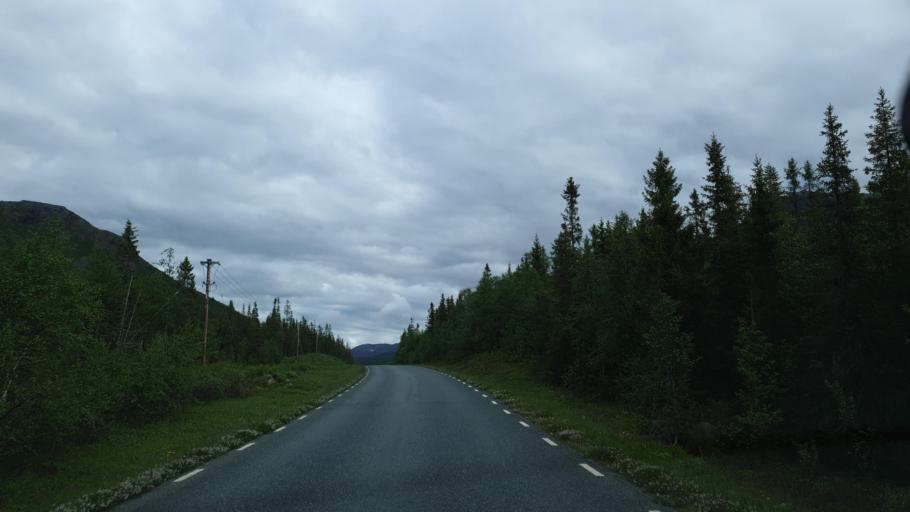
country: SE
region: Vaesterbotten
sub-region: Vilhelmina Kommun
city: Sjoberg
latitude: 65.2475
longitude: 15.4233
